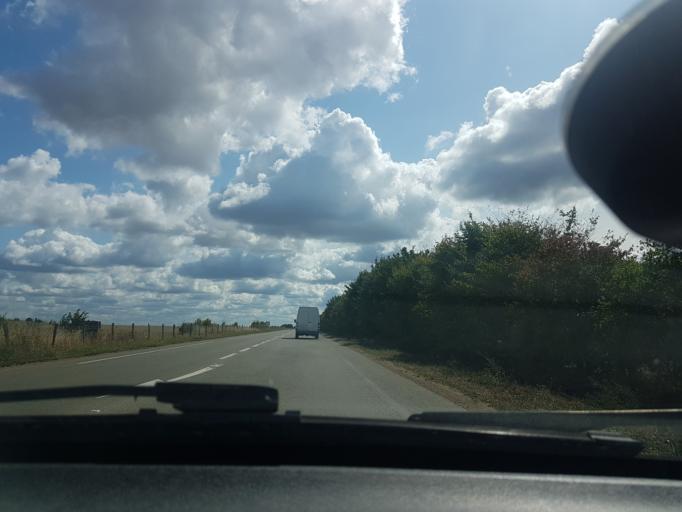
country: FR
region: Ile-de-France
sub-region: Departement des Yvelines
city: Plaisir
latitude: 48.8375
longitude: 1.9470
